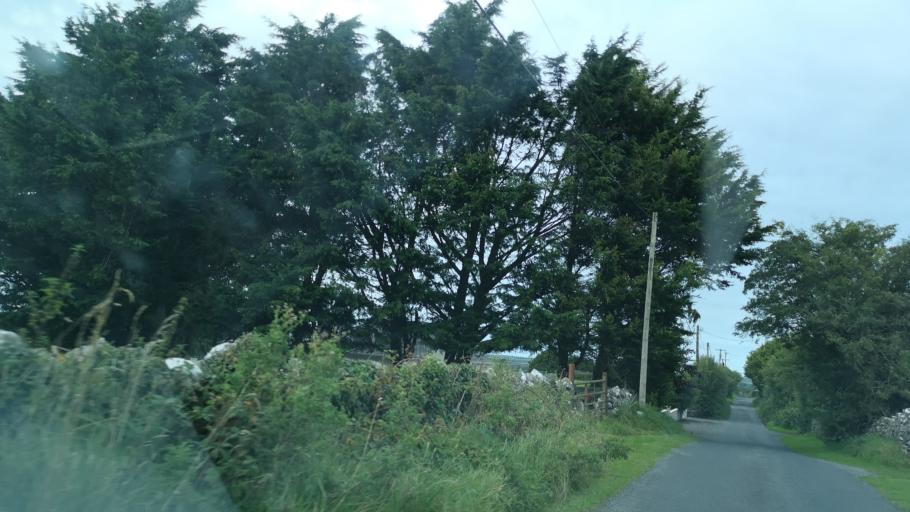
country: IE
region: Connaught
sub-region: County Galway
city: Ballinasloe
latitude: 53.3836
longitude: -8.1787
